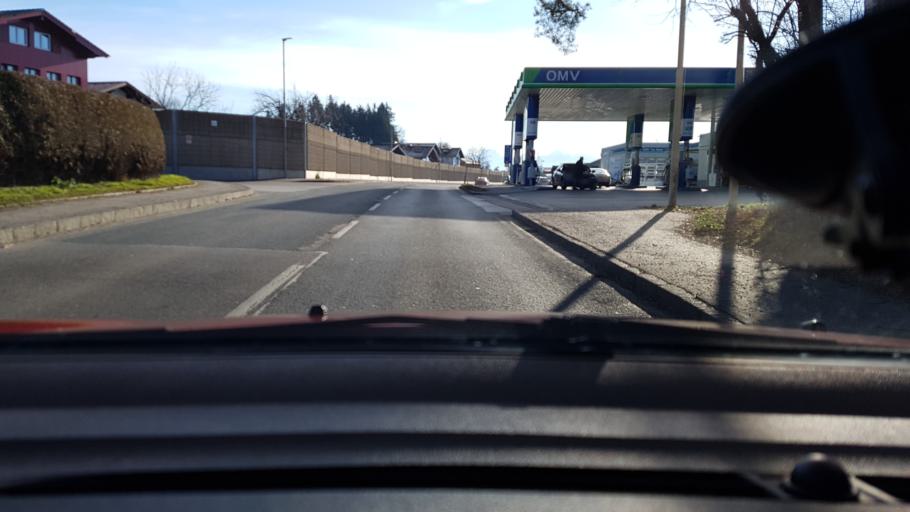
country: AT
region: Salzburg
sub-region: Politischer Bezirk Salzburg-Umgebung
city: Lamprechtshausen
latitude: 47.9870
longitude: 12.9546
